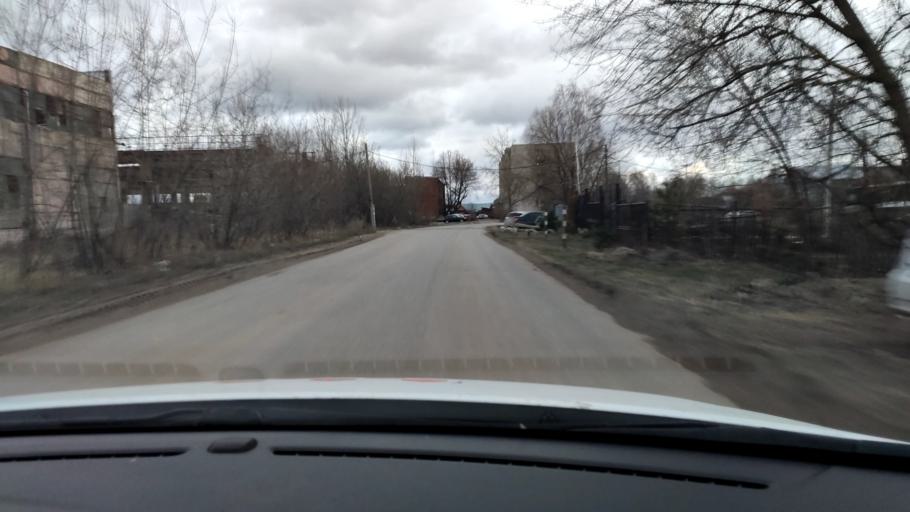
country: RU
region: Tatarstan
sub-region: Gorod Kazan'
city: Kazan
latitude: 55.7207
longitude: 49.0927
